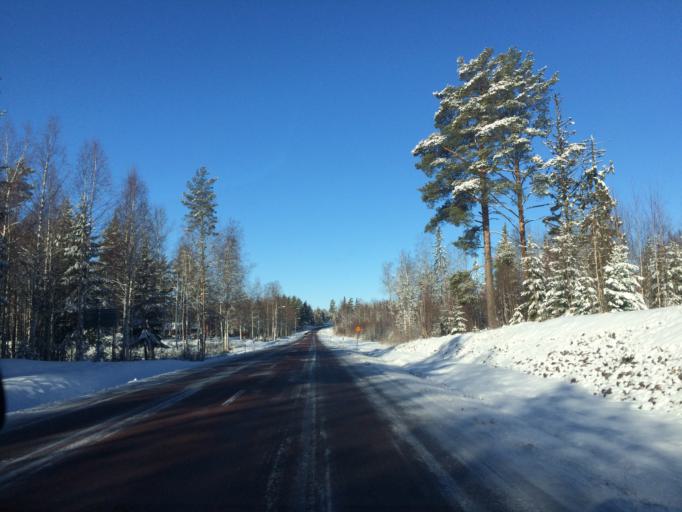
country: SE
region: Dalarna
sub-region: Vansbro Kommun
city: Vansbro
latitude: 60.8445
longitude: 14.1824
